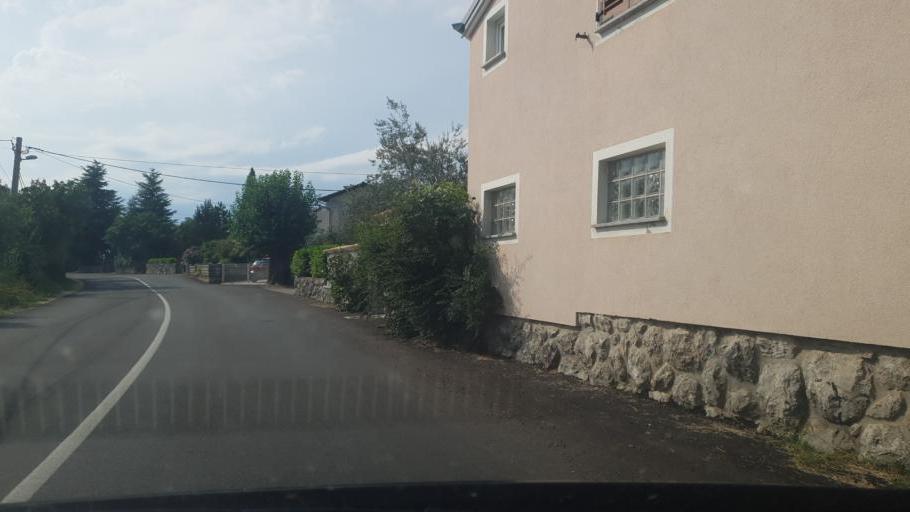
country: HR
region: Primorsko-Goranska
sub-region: Grad Crikvenica
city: Crikvenica
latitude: 45.1404
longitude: 14.6192
